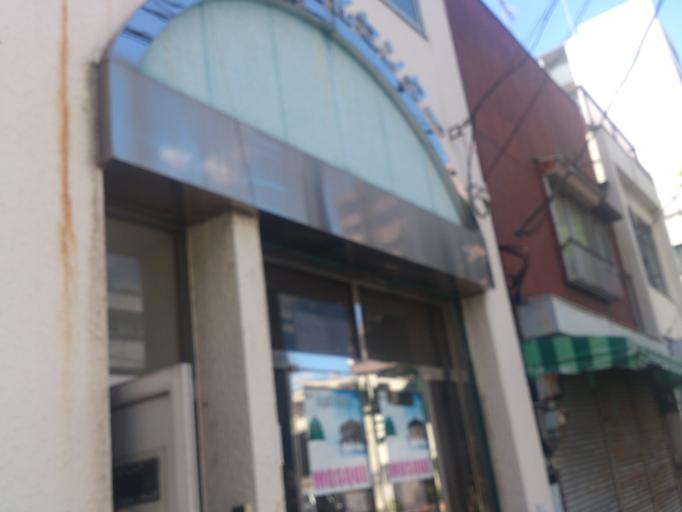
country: JP
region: Saitama
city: Soka
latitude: 35.7218
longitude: 139.8016
